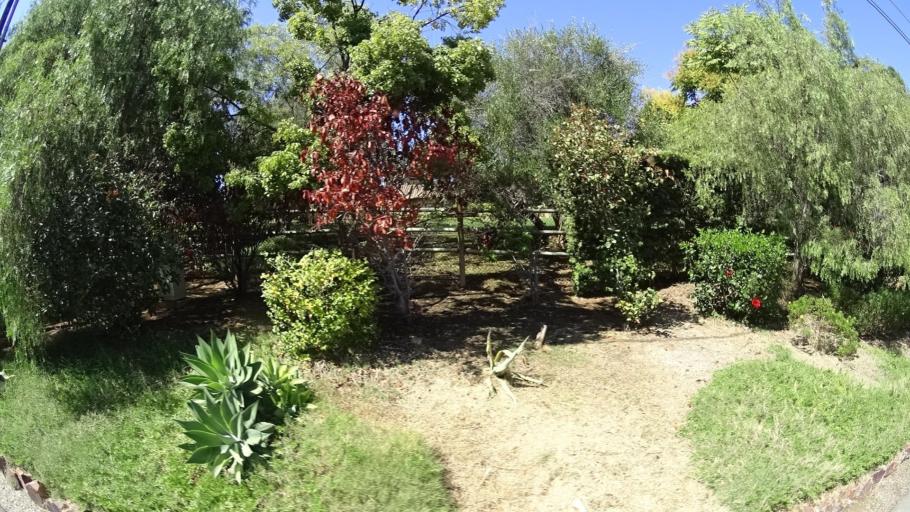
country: US
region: California
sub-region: San Diego County
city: Rancho Santa Fe
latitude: 33.0324
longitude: -117.1984
